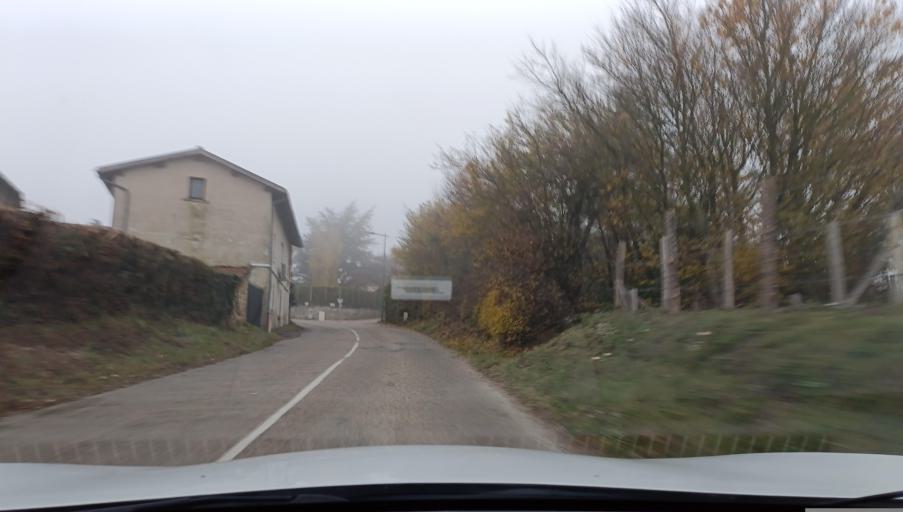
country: FR
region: Rhone-Alpes
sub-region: Departement de l'Isere
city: Serpaize
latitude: 45.5555
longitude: 4.9247
